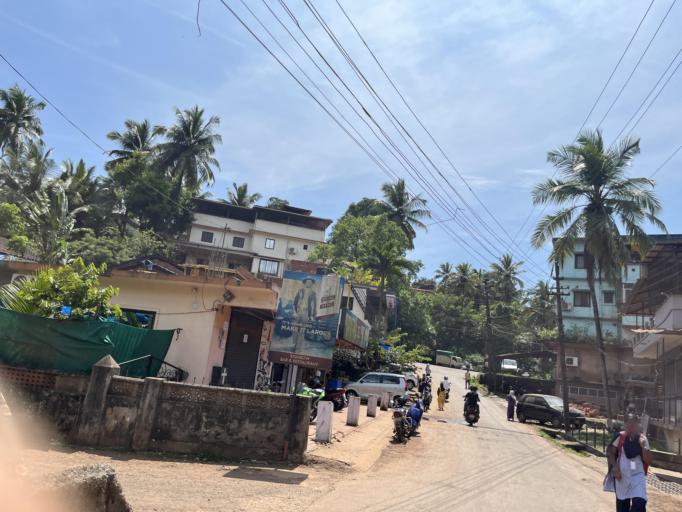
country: IN
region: Goa
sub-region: North Goa
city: Ponda
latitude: 15.4062
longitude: 74.0110
